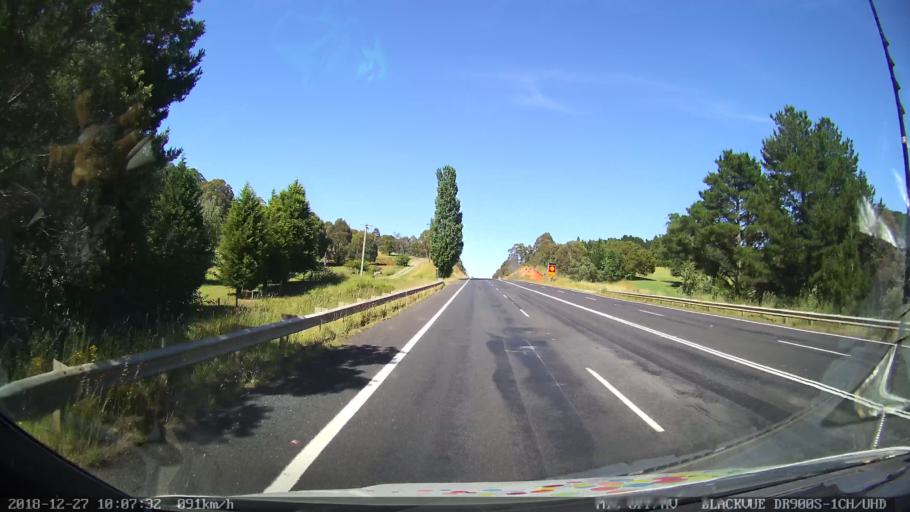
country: AU
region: New South Wales
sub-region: Lithgow
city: Portland
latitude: -33.4407
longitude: 149.8382
